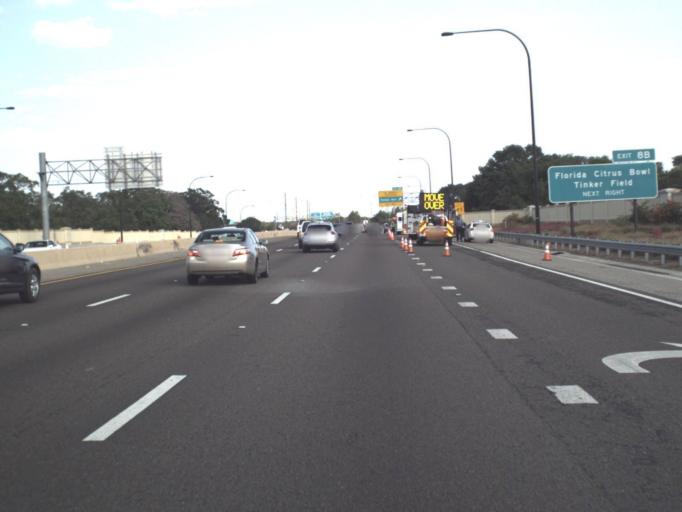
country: US
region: Florida
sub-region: Orange County
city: Orlando
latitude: 28.5392
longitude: -81.4094
